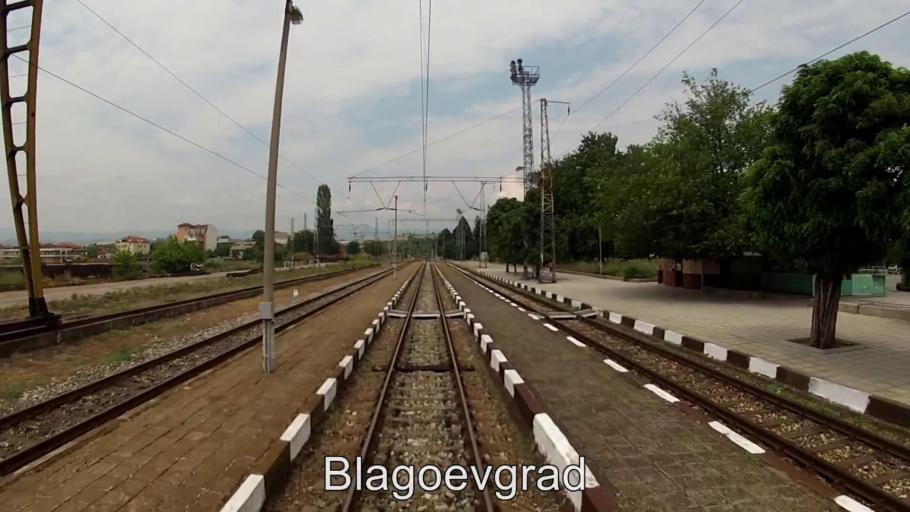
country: BG
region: Blagoevgrad
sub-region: Obshtina Blagoevgrad
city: Blagoevgrad
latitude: 42.0054
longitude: 23.0920
